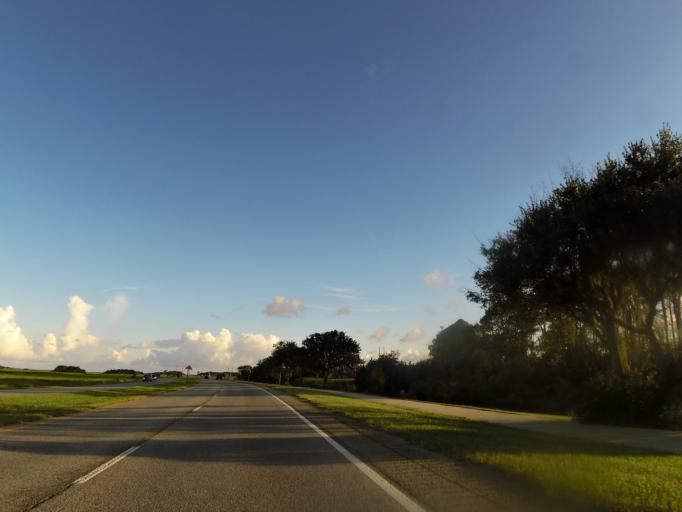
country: US
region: Georgia
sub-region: Glynn County
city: Brunswick
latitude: 31.1395
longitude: -81.4797
